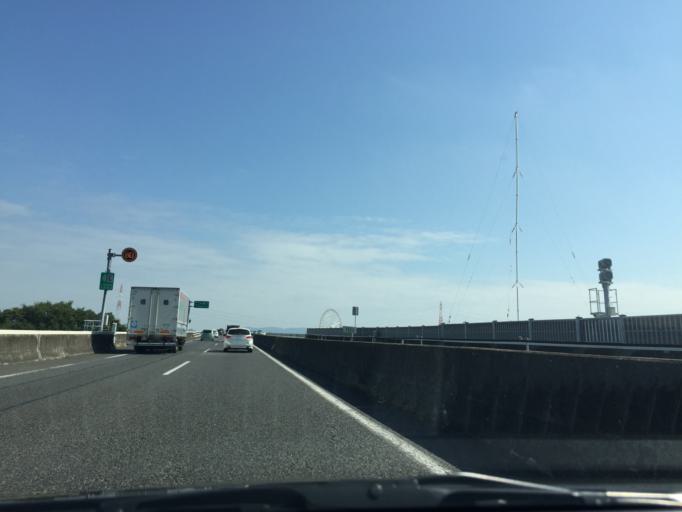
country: JP
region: Aichi
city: Kuroda
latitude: 35.3644
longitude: 136.8038
